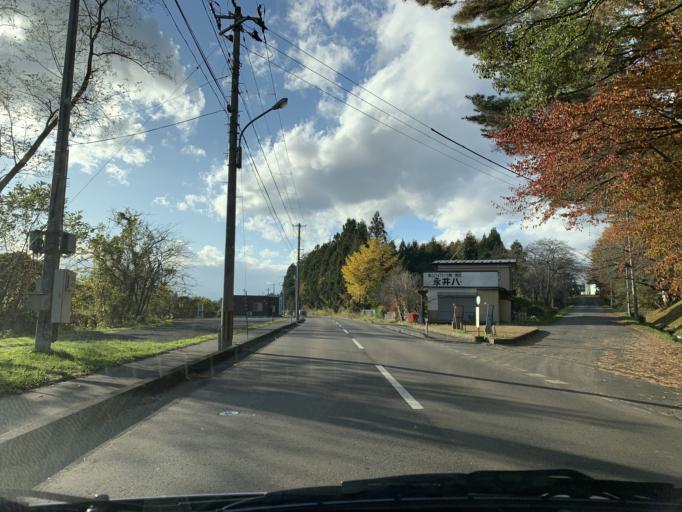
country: JP
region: Iwate
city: Mizusawa
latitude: 39.1185
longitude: 141.1026
